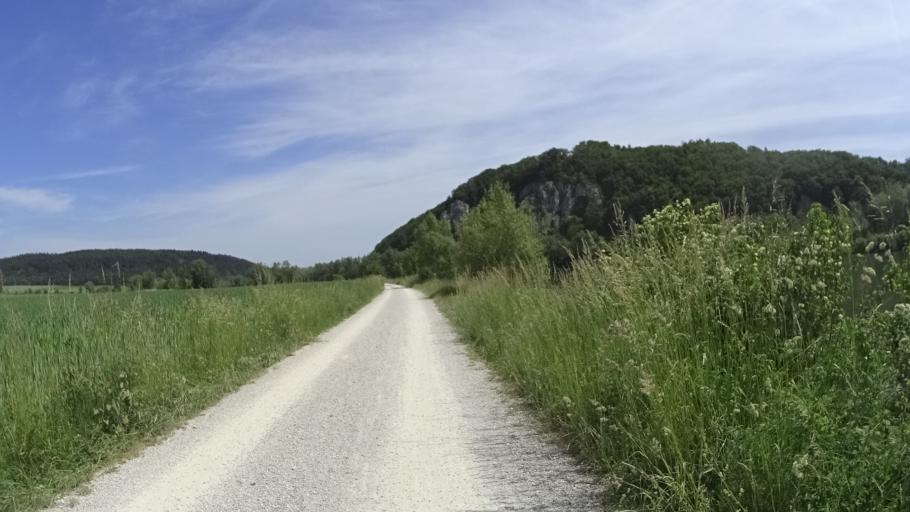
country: DE
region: Bavaria
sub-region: Lower Bavaria
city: Saal
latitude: 48.9101
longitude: 11.9681
